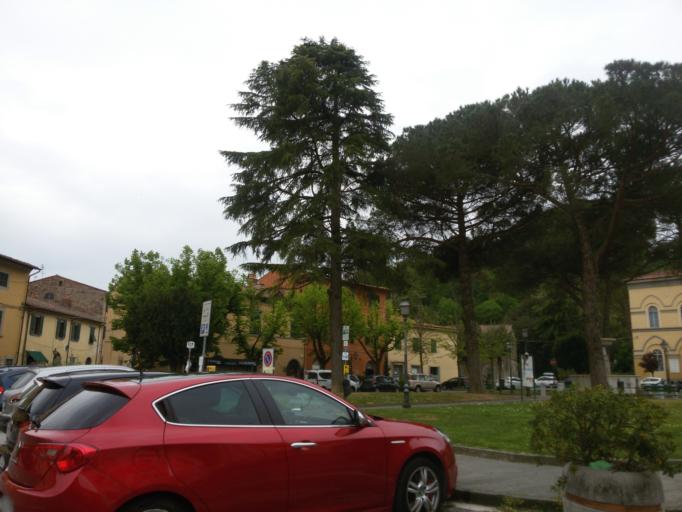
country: IT
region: Tuscany
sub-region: Province of Pisa
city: Vicopisano
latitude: 43.6995
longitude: 10.5840
